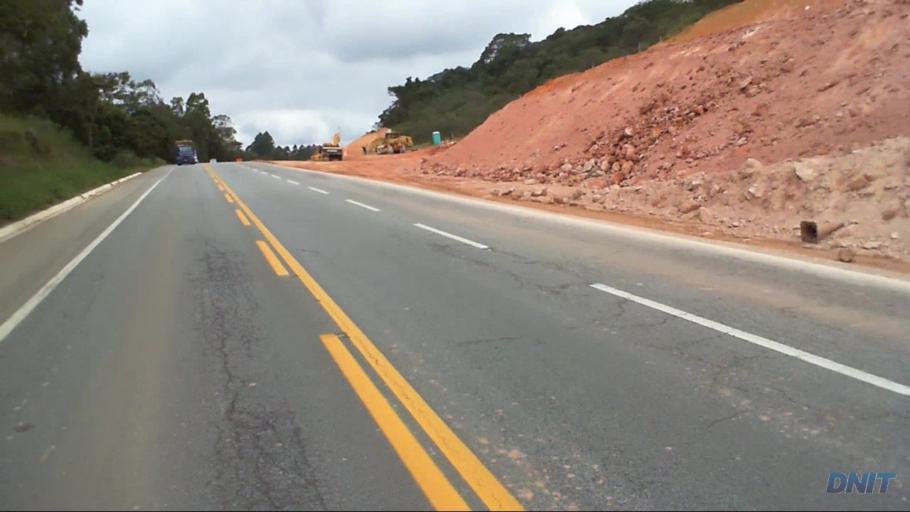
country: BR
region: Minas Gerais
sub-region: Caete
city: Caete
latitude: -19.7432
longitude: -43.5517
